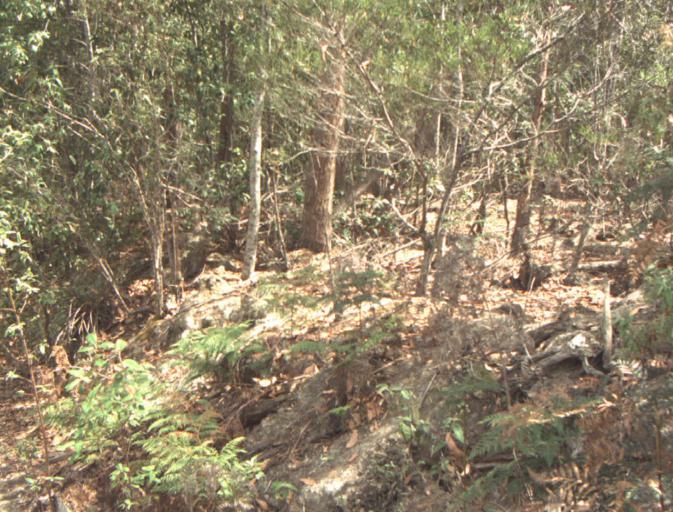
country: AU
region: Tasmania
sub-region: Launceston
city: Mayfield
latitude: -41.2040
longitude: 147.1568
